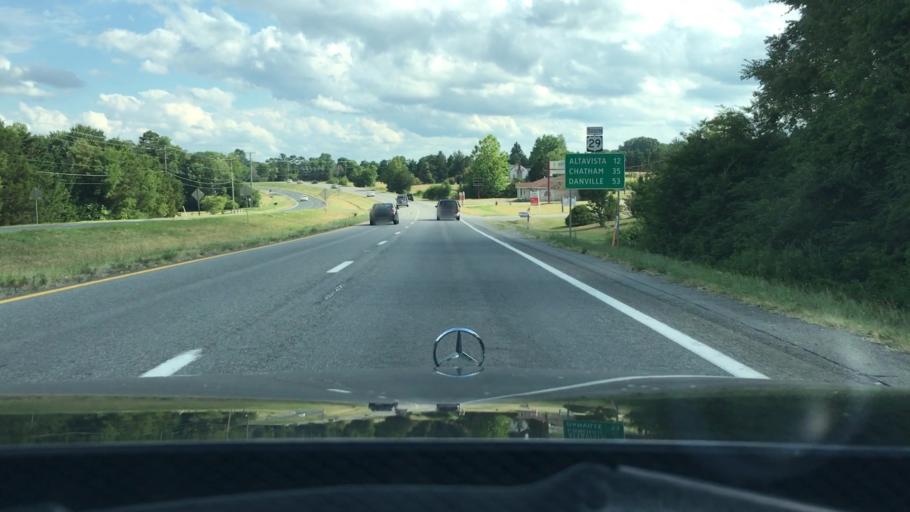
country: US
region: Virginia
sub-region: Campbell County
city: Rustburg
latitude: 37.2500
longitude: -79.1879
